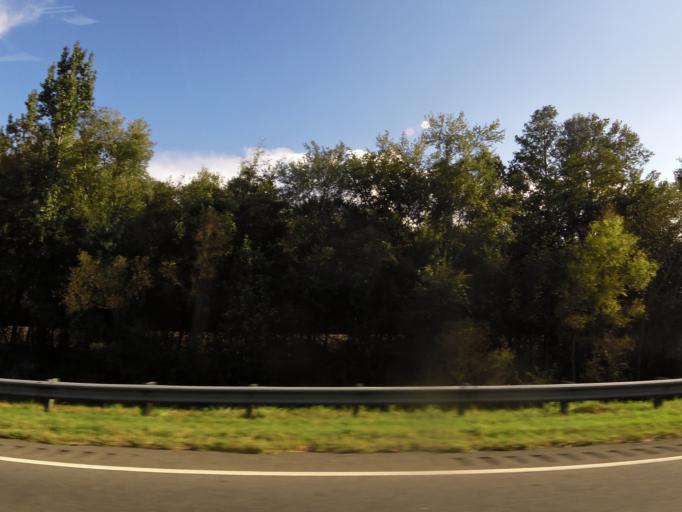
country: US
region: Georgia
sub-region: Brooks County
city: Quitman
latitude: 30.7940
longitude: -83.4444
